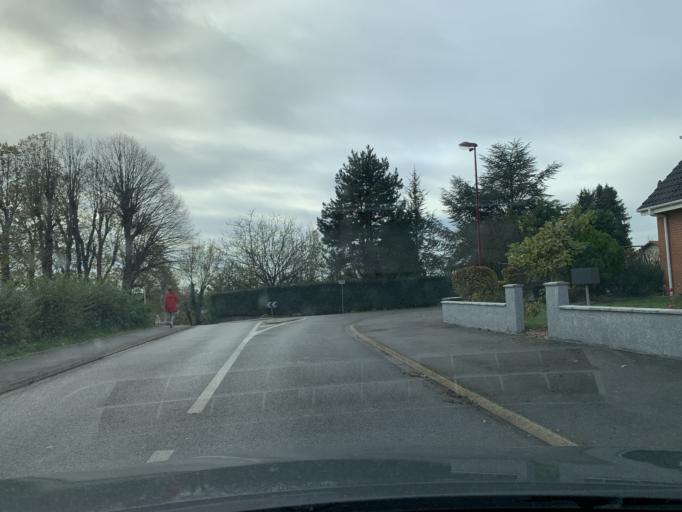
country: FR
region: Nord-Pas-de-Calais
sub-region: Departement du Nord
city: Neuville-Saint-Remy
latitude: 50.1848
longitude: 3.2156
